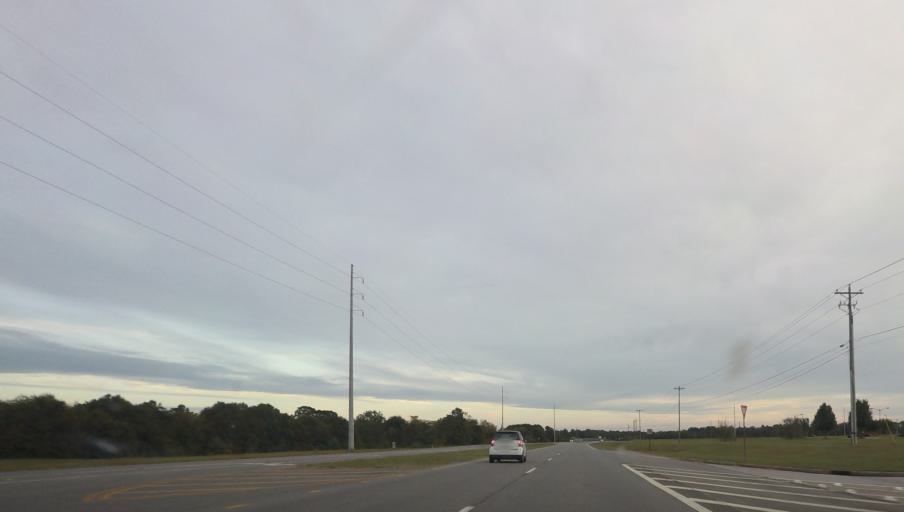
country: US
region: Georgia
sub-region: Houston County
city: Perry
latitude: 32.4695
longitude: -83.7001
